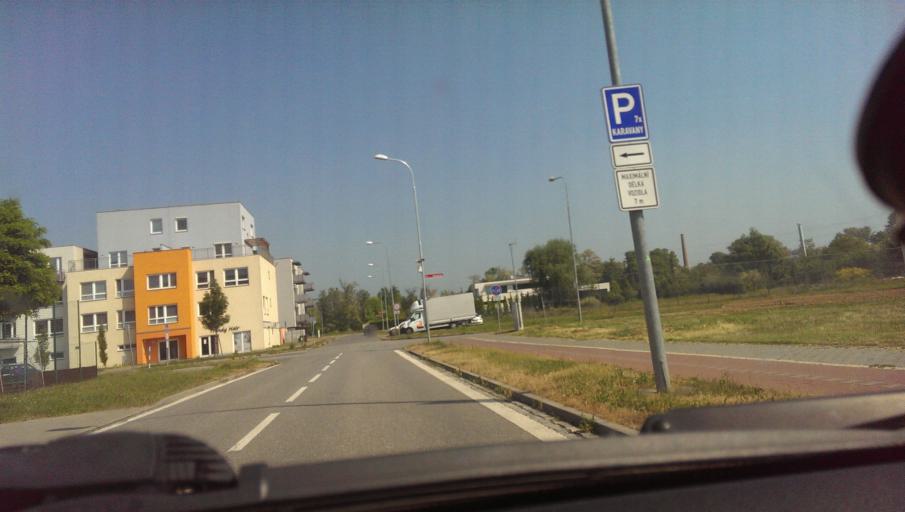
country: CZ
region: Zlin
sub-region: Okres Uherske Hradiste
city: Uherske Hradiste
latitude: 49.0713
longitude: 17.4732
